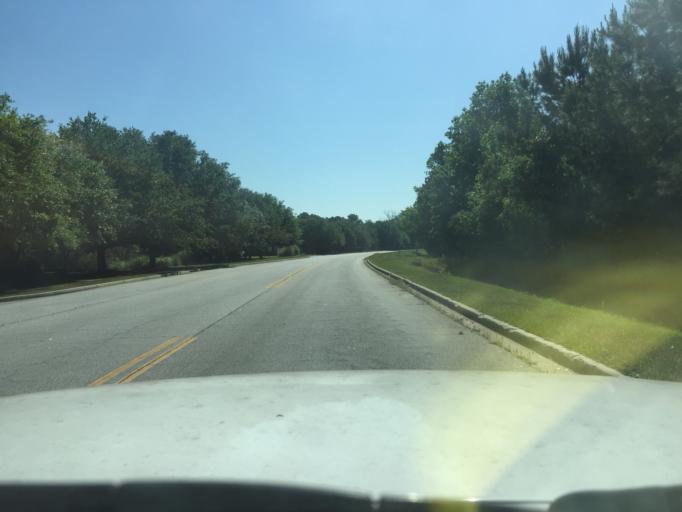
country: US
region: Georgia
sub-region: Chatham County
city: Georgetown
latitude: 32.0027
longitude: -81.2659
